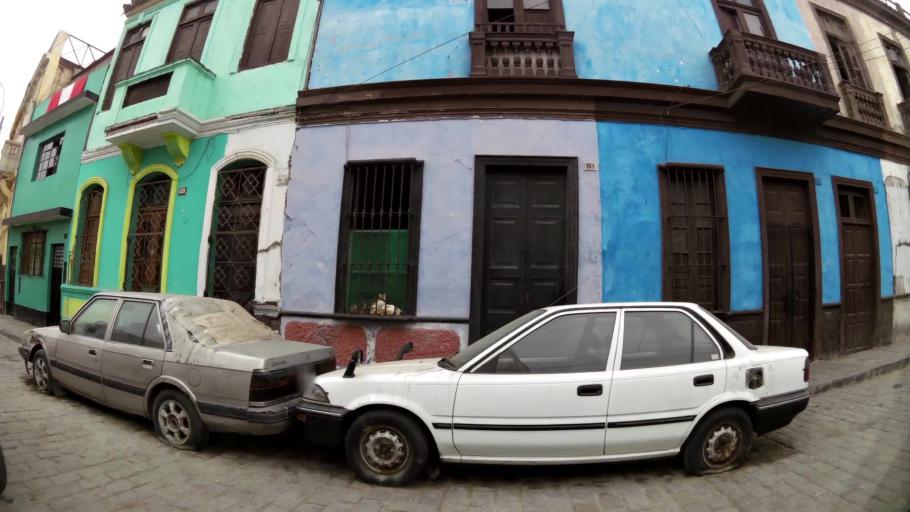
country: PE
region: Callao
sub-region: Callao
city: Callao
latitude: -12.0586
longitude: -77.1447
